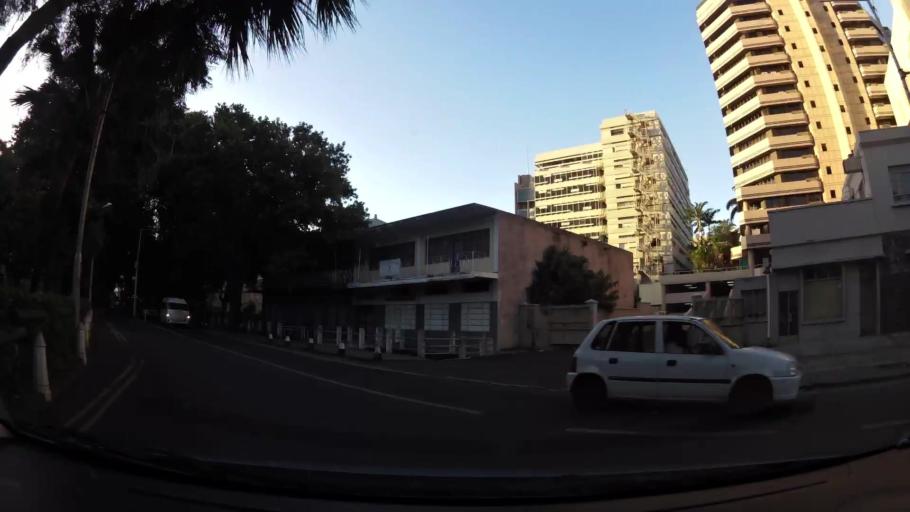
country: MU
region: Port Louis
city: Port Louis
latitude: -20.1642
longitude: 57.5027
